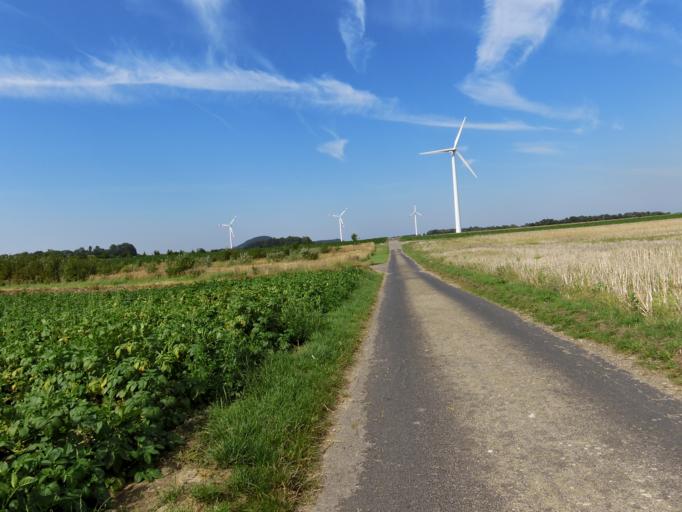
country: DE
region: North Rhine-Westphalia
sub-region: Regierungsbezirk Koln
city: Alsdorf
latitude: 50.8926
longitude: 6.1644
